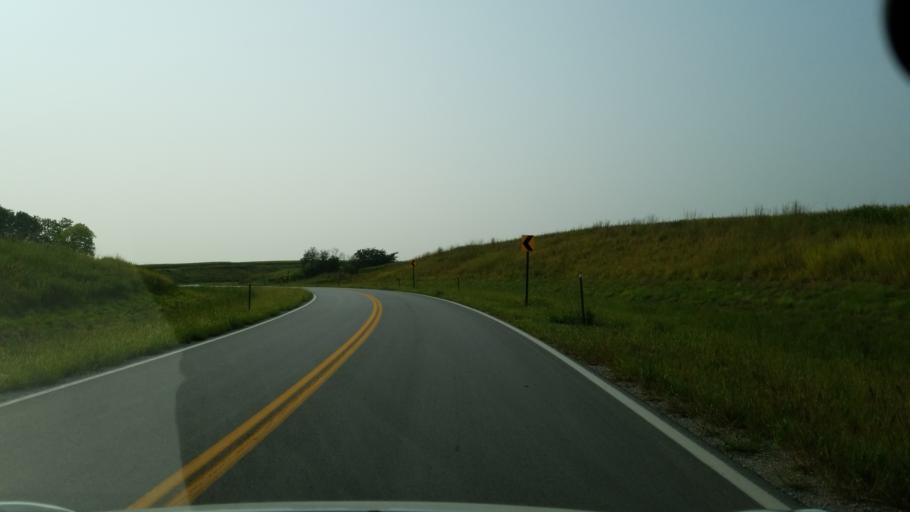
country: US
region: Nebraska
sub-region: Sarpy County
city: Offutt Air Force Base
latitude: 41.0800
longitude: -95.9318
